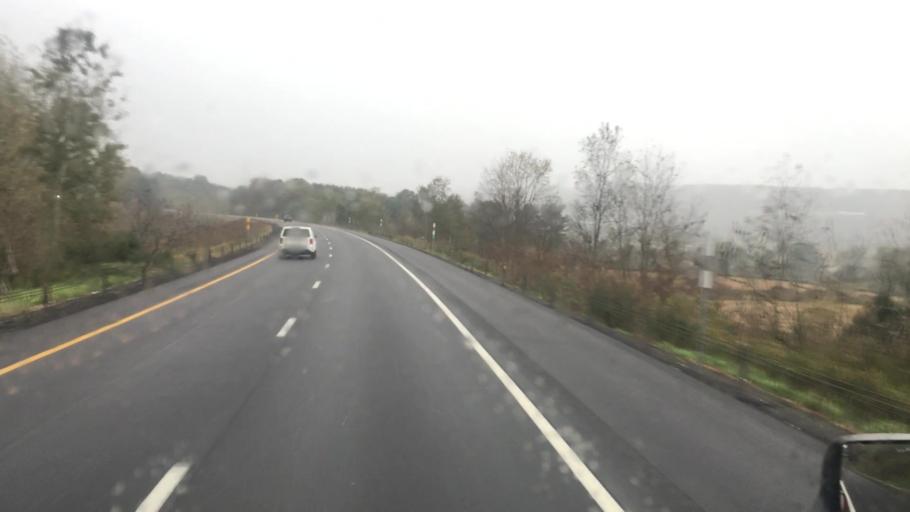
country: US
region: New York
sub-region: Chenango County
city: Bainbridge
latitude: 42.1986
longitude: -75.5702
